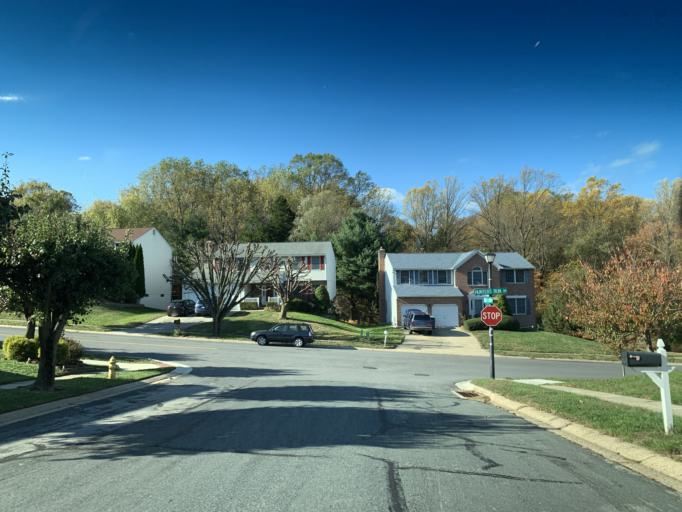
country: US
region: Maryland
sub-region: Harford County
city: Bel Air South
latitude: 39.5017
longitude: -76.3145
